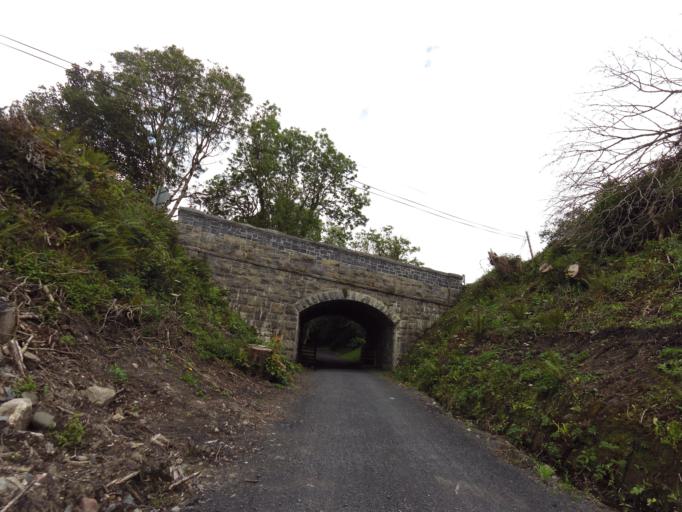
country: IE
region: Connaught
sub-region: Maigh Eo
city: Westport
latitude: 53.8128
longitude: -9.5350
